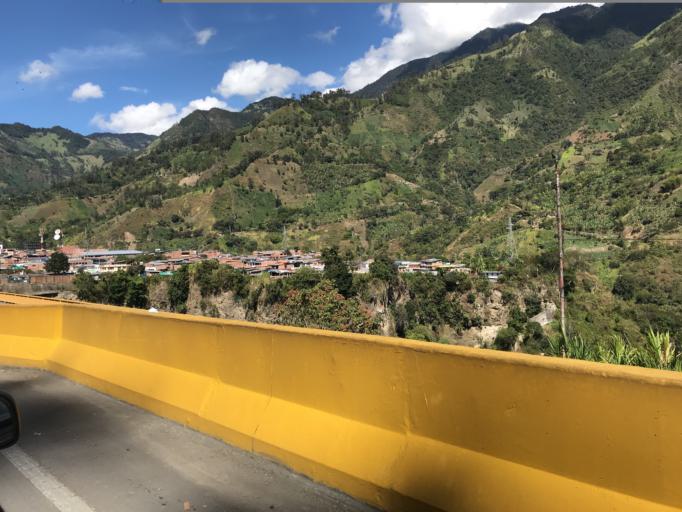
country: CO
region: Tolima
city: Cajamarca
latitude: 4.4415
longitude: -75.4219
